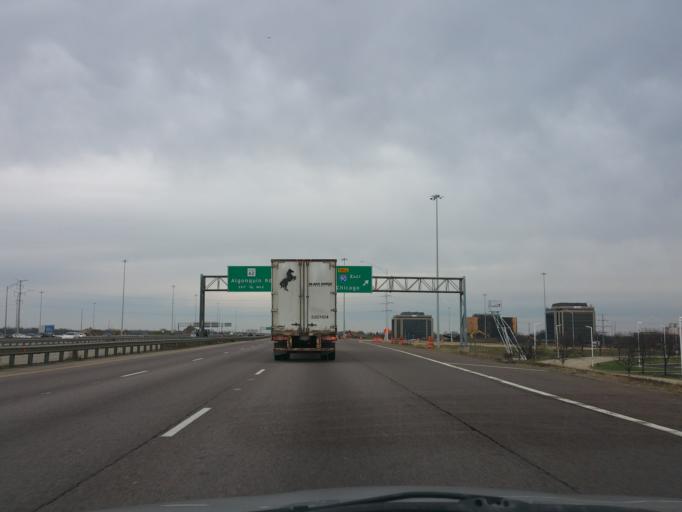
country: US
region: Illinois
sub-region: Cook County
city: Rolling Meadows
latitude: 42.0523
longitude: -88.0284
